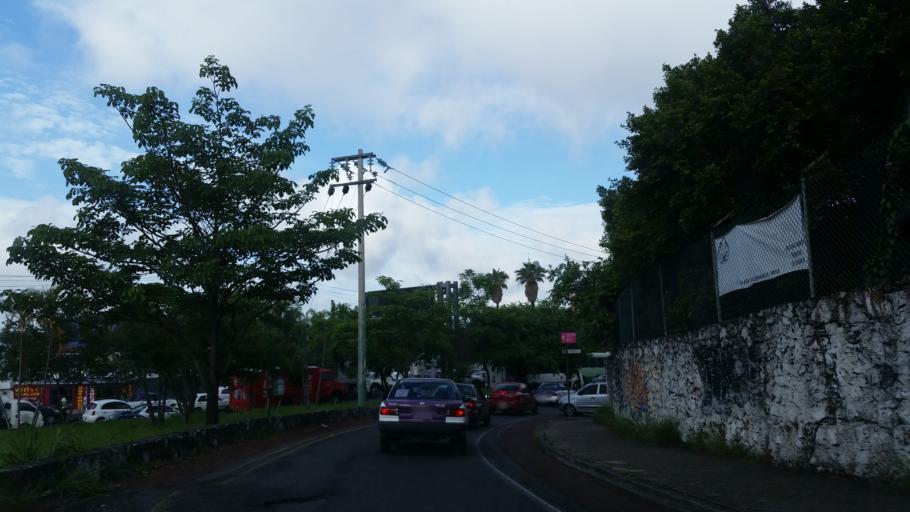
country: MX
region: Morelos
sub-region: Cuernavaca
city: Cuernavaca
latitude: 18.9216
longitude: -99.2036
